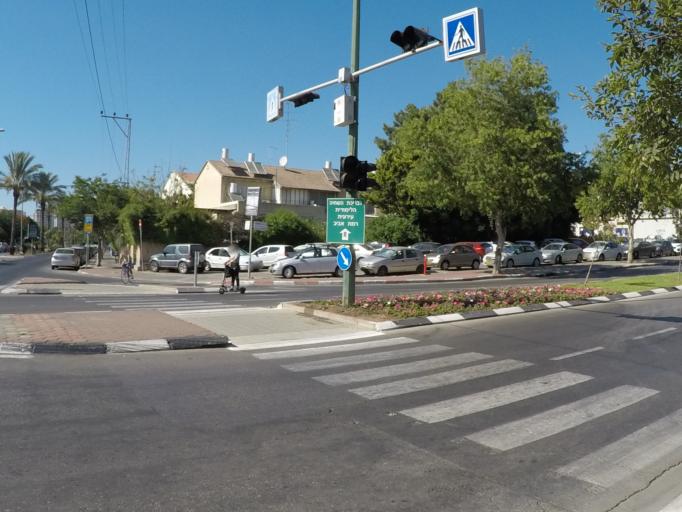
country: IL
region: Tel Aviv
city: Ramat Gan
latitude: 32.1028
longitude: 34.7948
